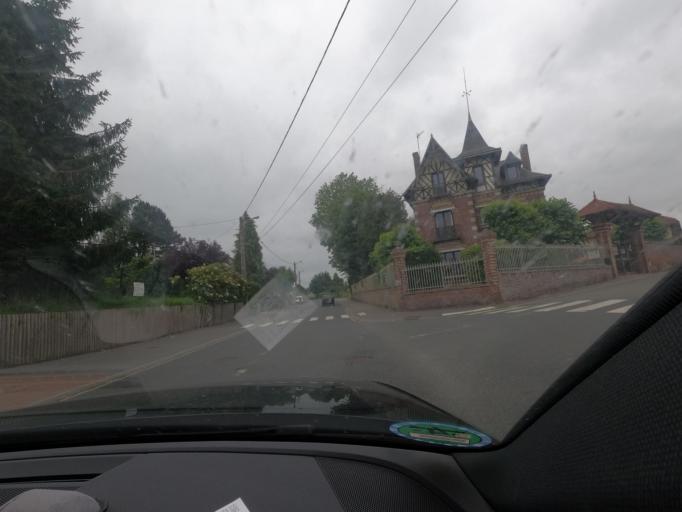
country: FR
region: Picardie
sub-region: Departement de l'Oise
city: Ressons-sur-Matz
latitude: 49.5388
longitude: 2.7390
